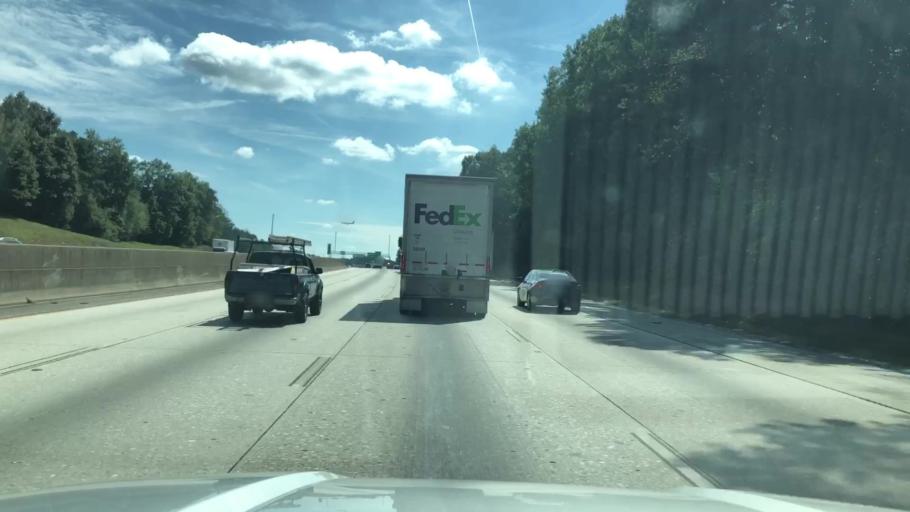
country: US
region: Georgia
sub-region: Fulton County
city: College Park
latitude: 33.6420
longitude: -84.4959
